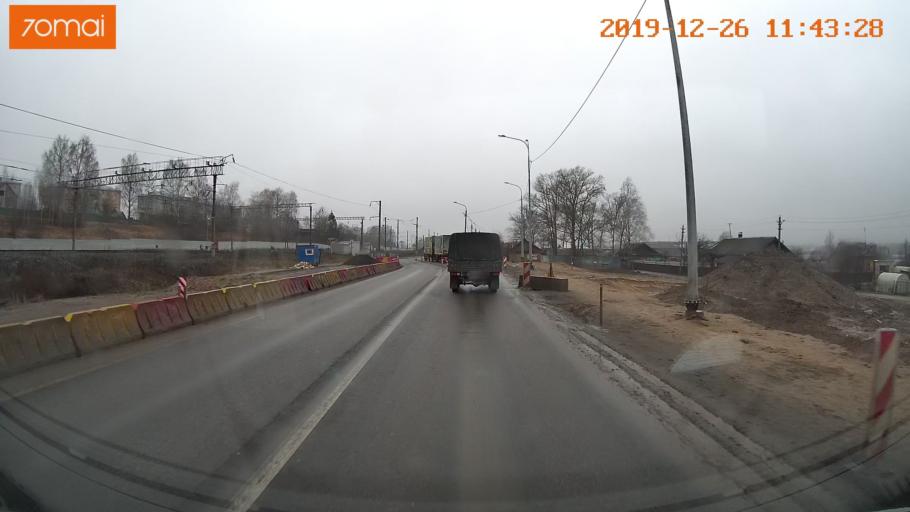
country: RU
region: Vologda
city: Sheksna
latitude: 59.2099
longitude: 38.5070
